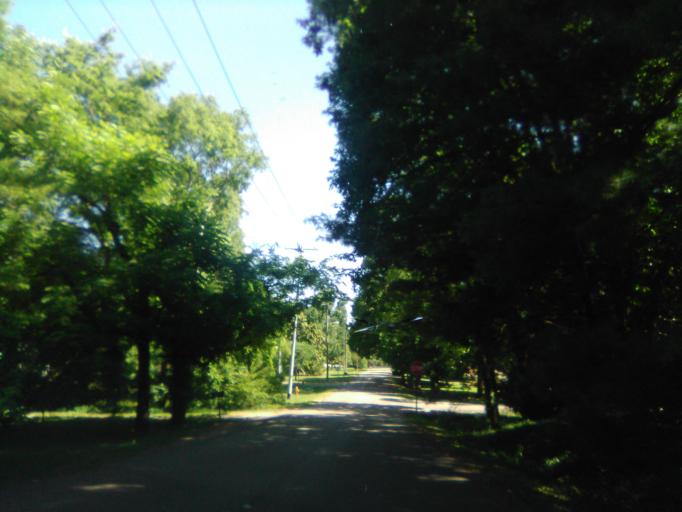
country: US
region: Tennessee
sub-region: Davidson County
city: Belle Meade
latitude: 36.1188
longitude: -86.8306
